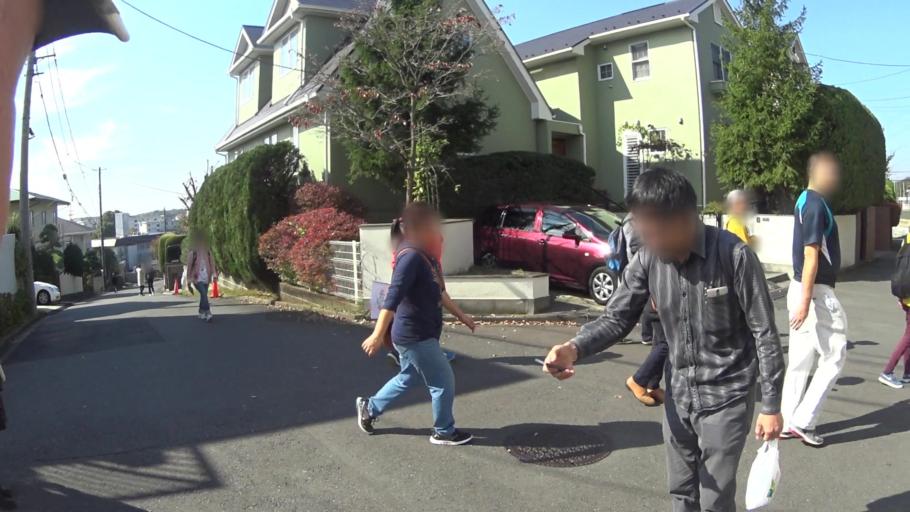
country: JP
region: Tokyo
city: Chofugaoka
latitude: 35.5852
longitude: 139.5557
